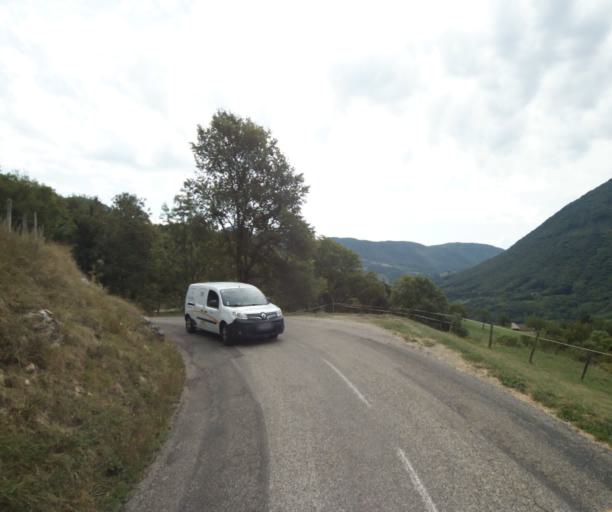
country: FR
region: Rhone-Alpes
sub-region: Departement de l'Isere
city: Saint-Egreve
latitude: 45.2592
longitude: 5.7082
